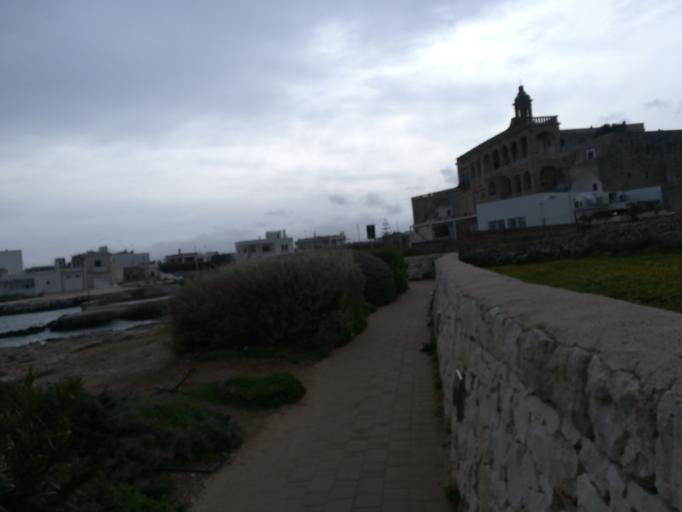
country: IT
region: Apulia
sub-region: Provincia di Bari
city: Polignano a Mare
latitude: 41.0144
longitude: 17.1929
